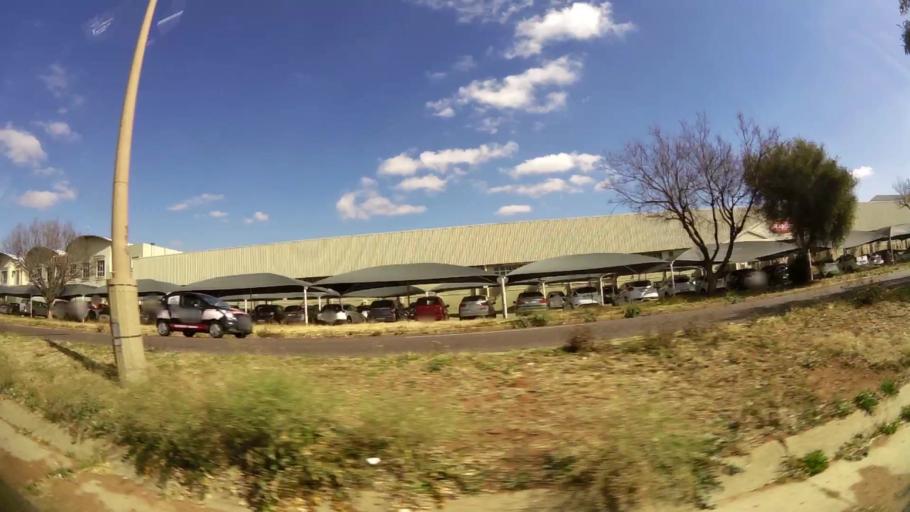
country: ZA
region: Gauteng
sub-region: West Rand District Municipality
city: Krugersdorp
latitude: -26.1162
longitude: 27.8167
